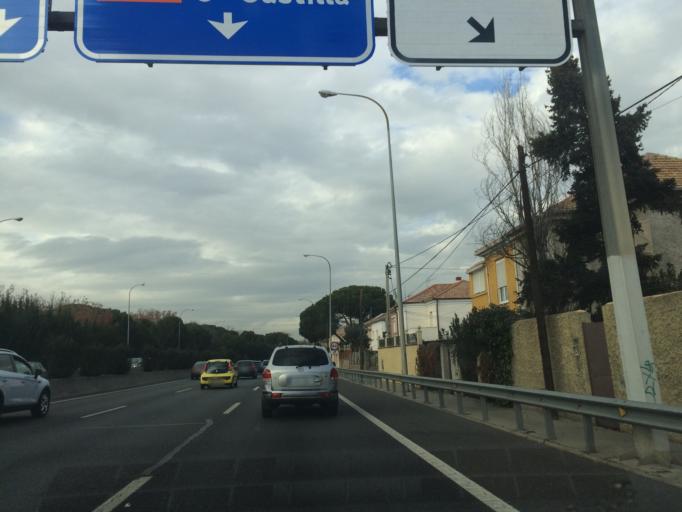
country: ES
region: Madrid
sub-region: Provincia de Madrid
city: Moncloa-Aravaca
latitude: 40.4286
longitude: -3.7356
